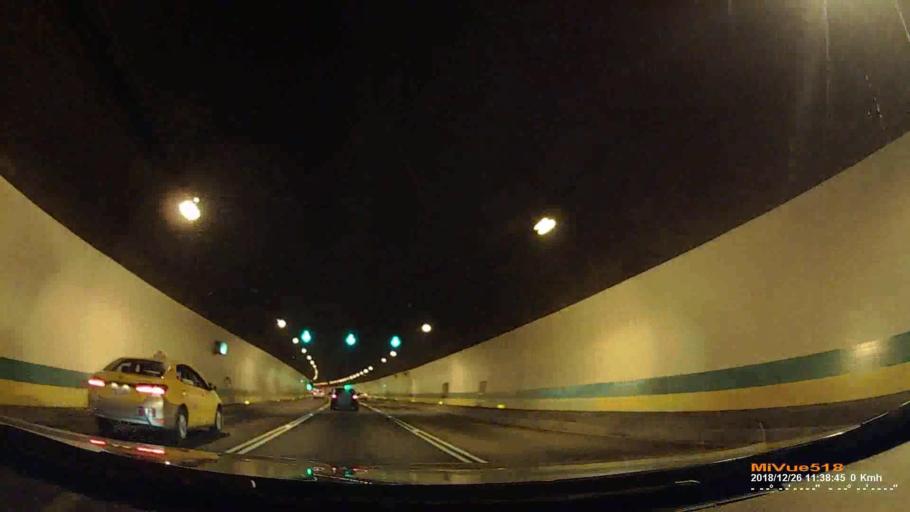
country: TW
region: Taipei
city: Taipei
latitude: 24.9837
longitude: 121.5870
